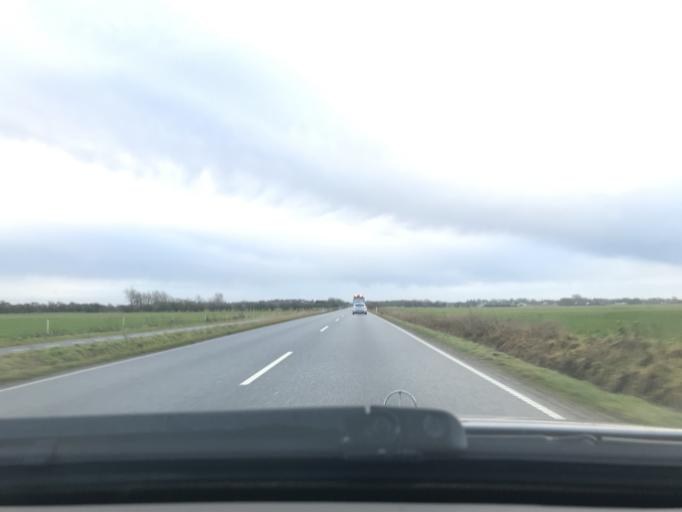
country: DK
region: South Denmark
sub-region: Esbjerg Kommune
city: Ribe
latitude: 55.2473
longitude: 8.7233
